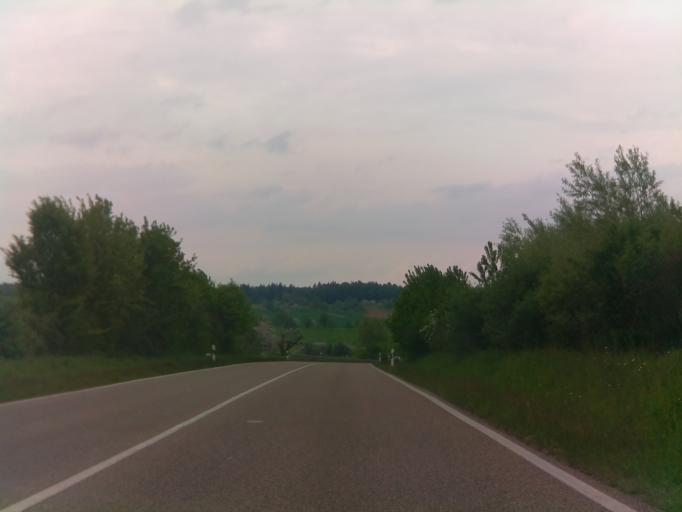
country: DE
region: Baden-Wuerttemberg
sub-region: Tuebingen Region
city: Pliezhausen
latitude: 48.5852
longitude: 9.1703
